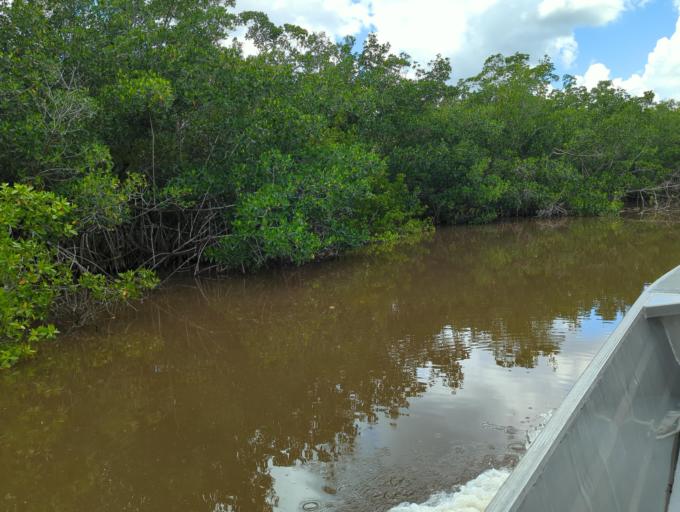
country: US
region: Florida
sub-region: Collier County
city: Marco
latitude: 25.9109
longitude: -81.3662
